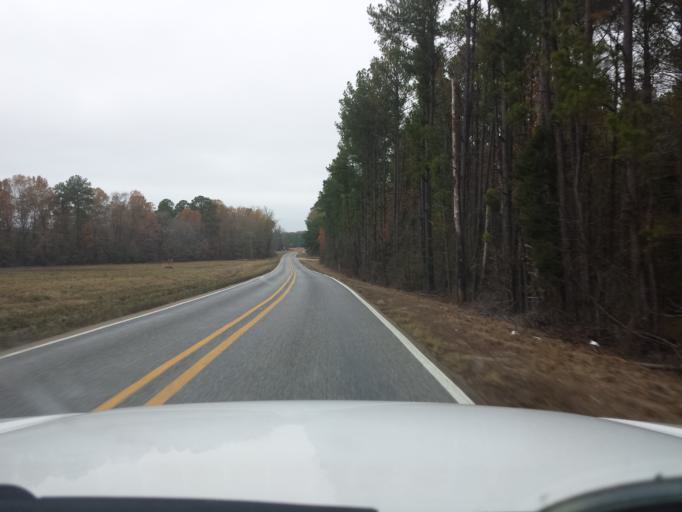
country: US
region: Mississippi
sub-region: Madison County
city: Canton
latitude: 32.4818
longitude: -89.9173
